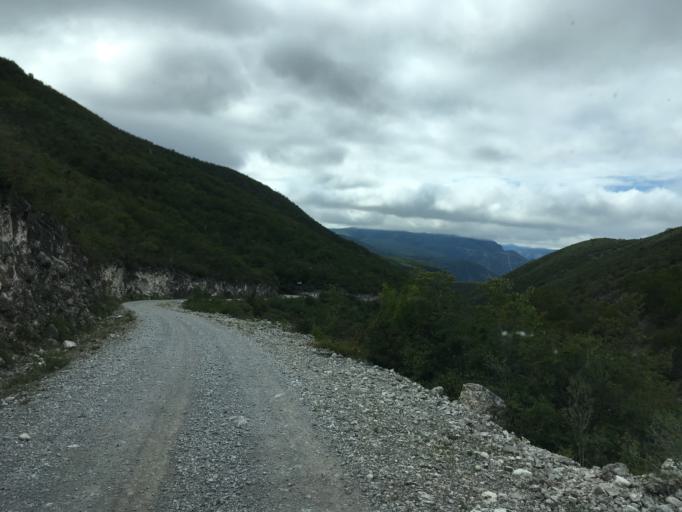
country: MX
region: Hidalgo
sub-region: Metztitlan
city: Fontezuelas
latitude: 20.6230
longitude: -98.8697
